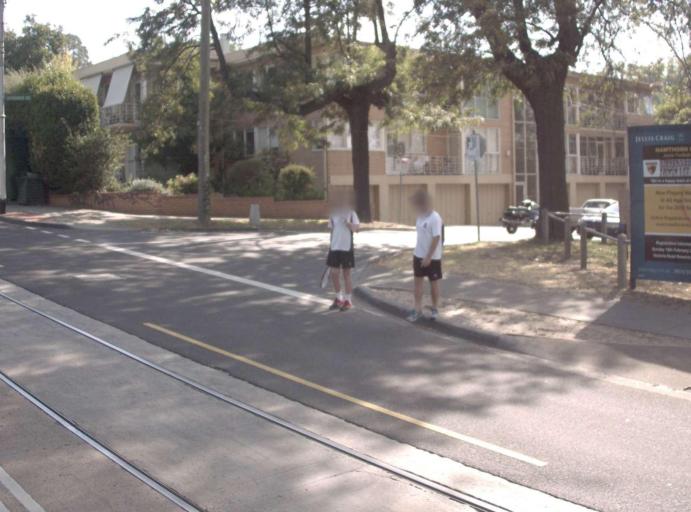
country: AU
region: Victoria
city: Glenferrie
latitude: -37.8357
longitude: 145.0330
